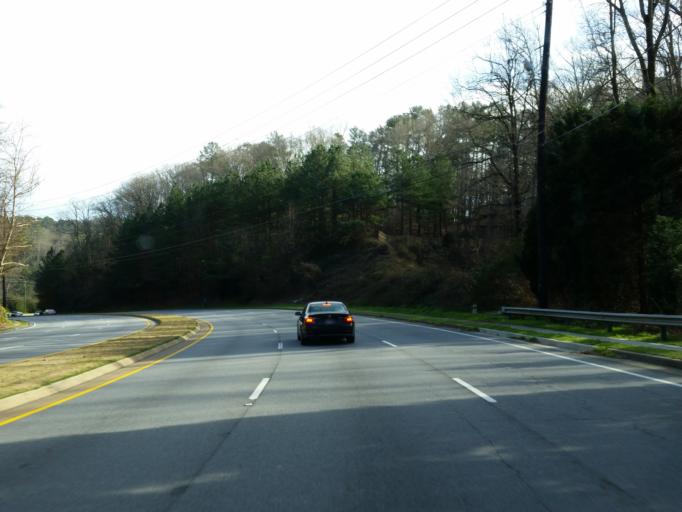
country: US
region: Georgia
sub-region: Fulton County
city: Sandy Springs
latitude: 33.9479
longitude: -84.4102
